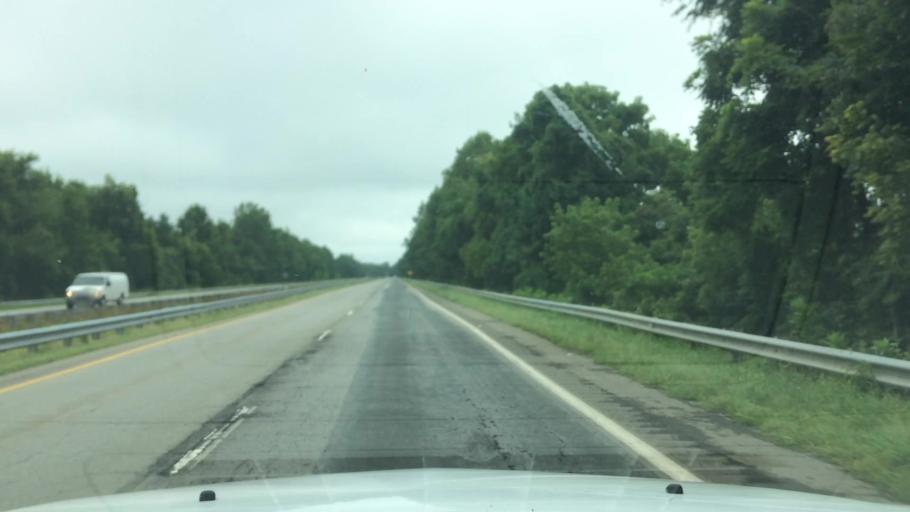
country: US
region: North Carolina
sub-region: Forsyth County
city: Lewisville
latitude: 36.1040
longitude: -80.5097
